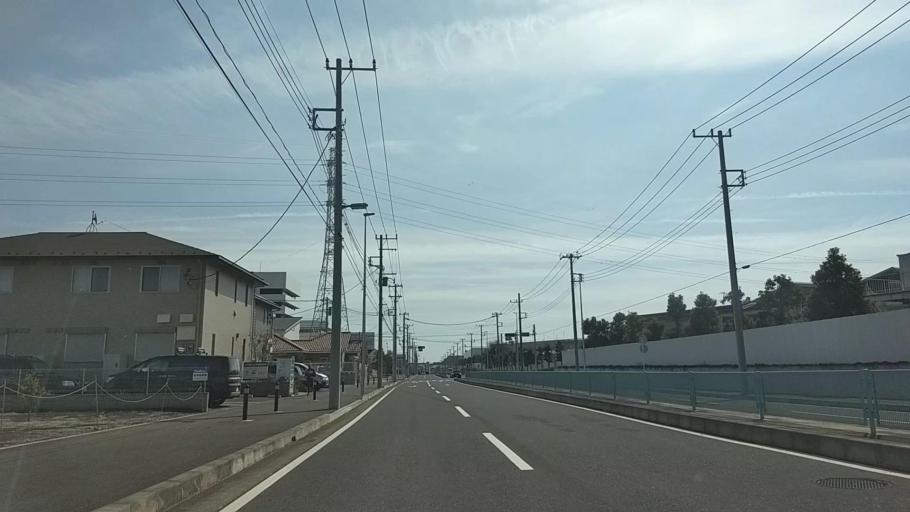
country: JP
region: Kanagawa
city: Fujisawa
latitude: 35.4012
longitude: 139.4557
